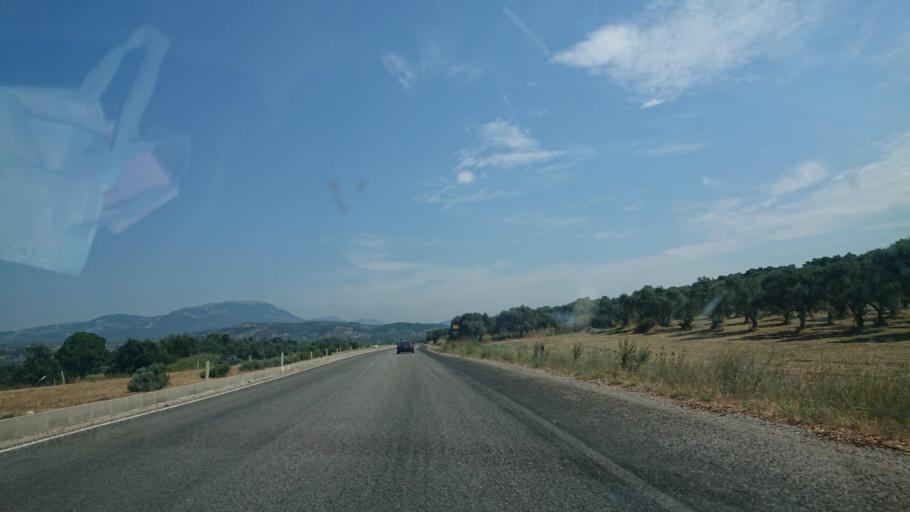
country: TR
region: Izmir
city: Dagkizilca
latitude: 38.2346
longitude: 27.3735
